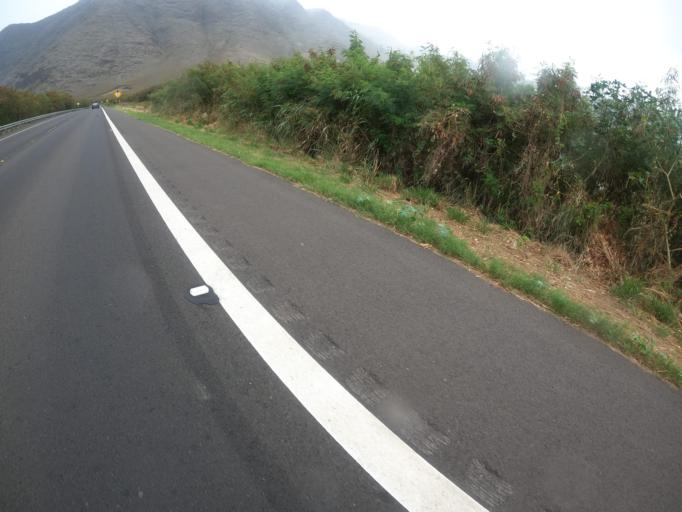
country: US
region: Hawaii
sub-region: Honolulu County
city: Makaha Valley
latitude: 21.5317
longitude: -158.2279
